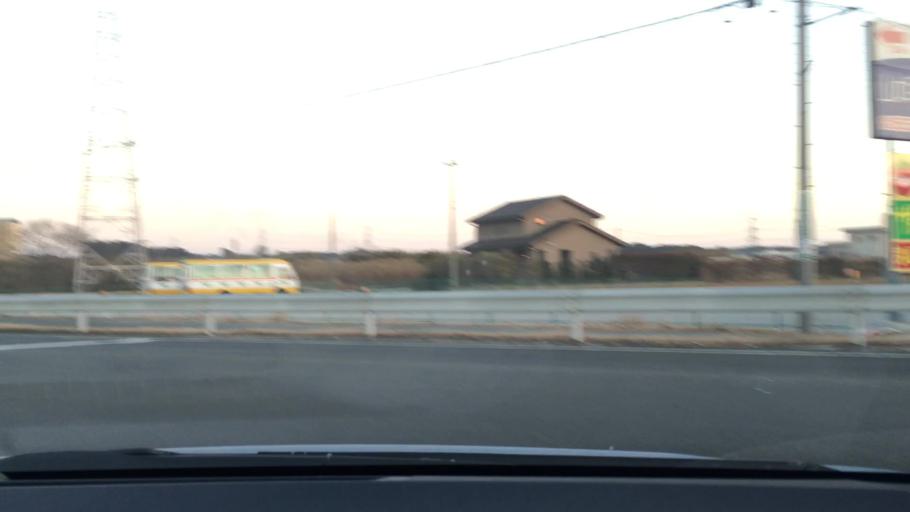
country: JP
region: Aichi
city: Tahara
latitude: 34.6607
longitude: 137.2669
